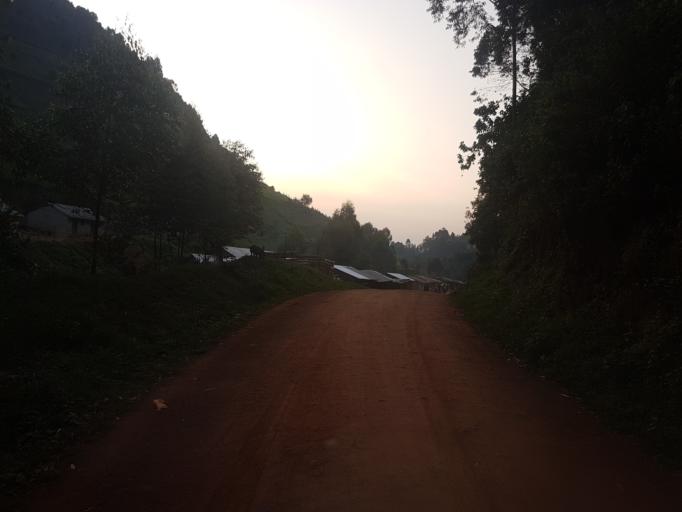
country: UG
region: Western Region
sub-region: Kanungu District
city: Kanungu
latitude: -0.9713
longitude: 29.8412
